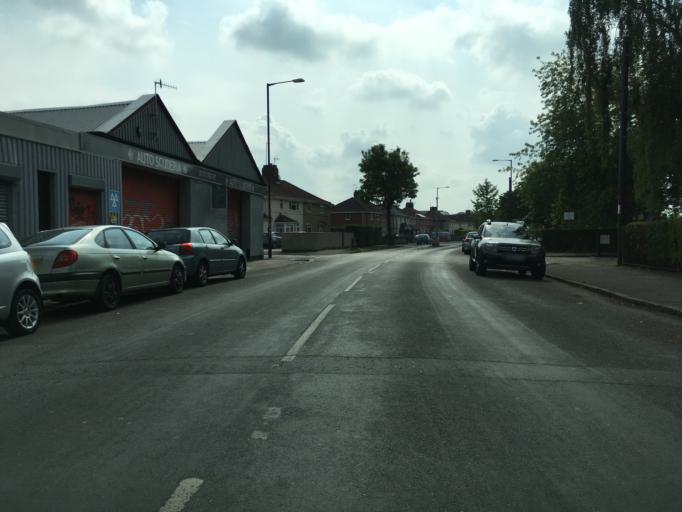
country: GB
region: England
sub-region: Bristol
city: Bristol
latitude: 51.4412
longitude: -2.6183
